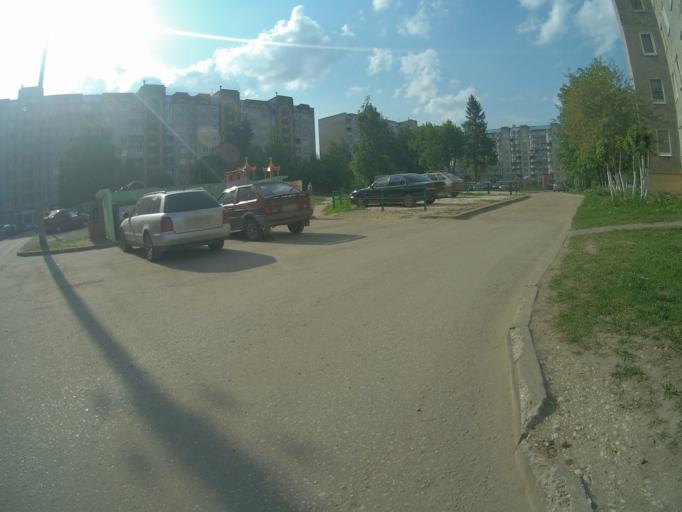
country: RU
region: Vladimir
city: Kommunar
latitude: 56.1681
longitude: 40.4478
